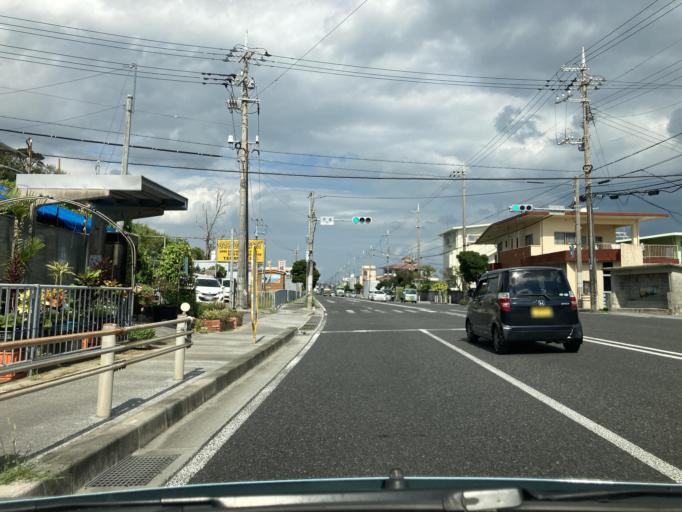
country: JP
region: Okinawa
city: Ginowan
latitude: 26.2386
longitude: 127.7764
